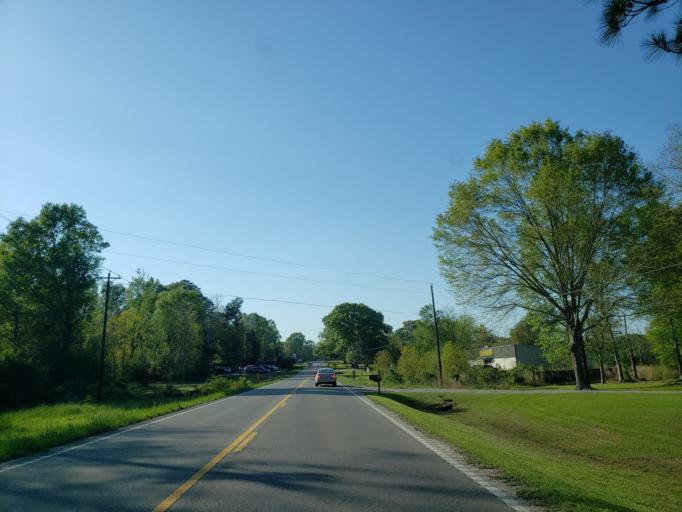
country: US
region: Mississippi
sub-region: Jones County
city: Laurel
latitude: 31.6487
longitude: -89.1010
